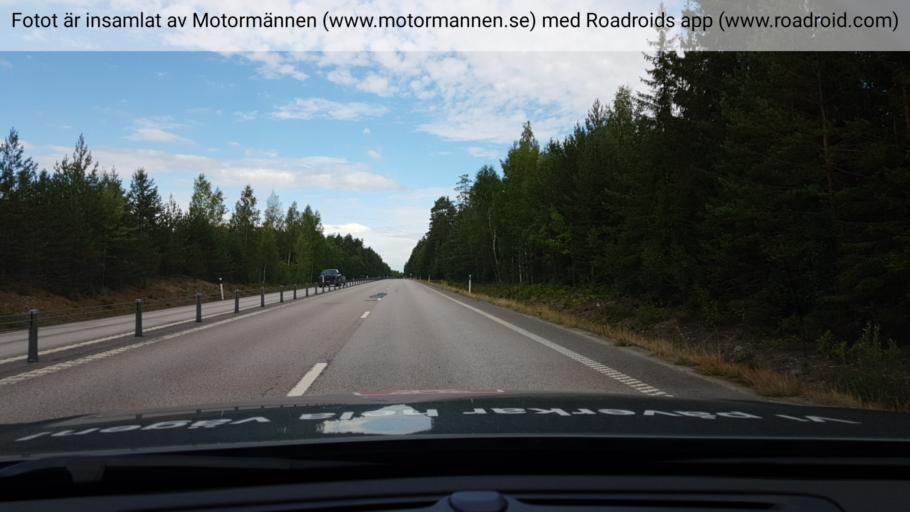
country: SE
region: Uppsala
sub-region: Heby Kommun
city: Tarnsjo
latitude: 60.2621
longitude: 16.9465
